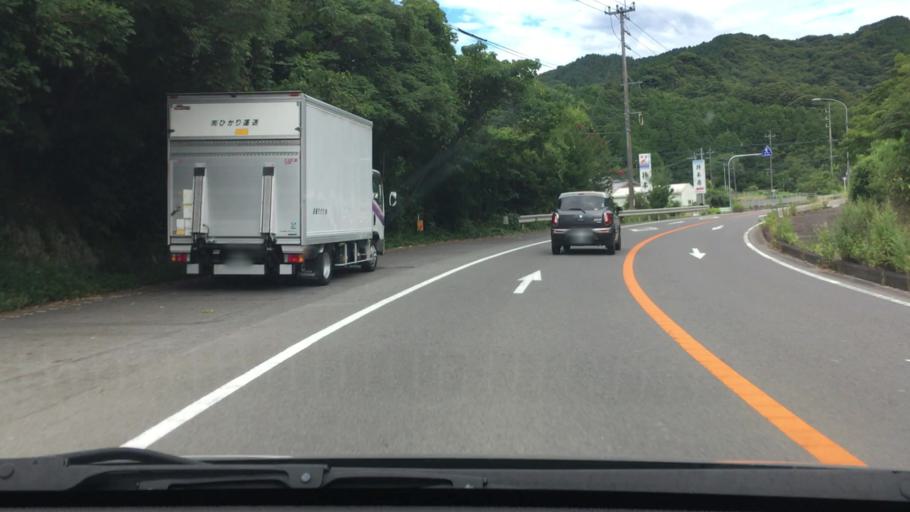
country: JP
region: Nagasaki
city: Sasebo
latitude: 32.9875
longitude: 129.7441
